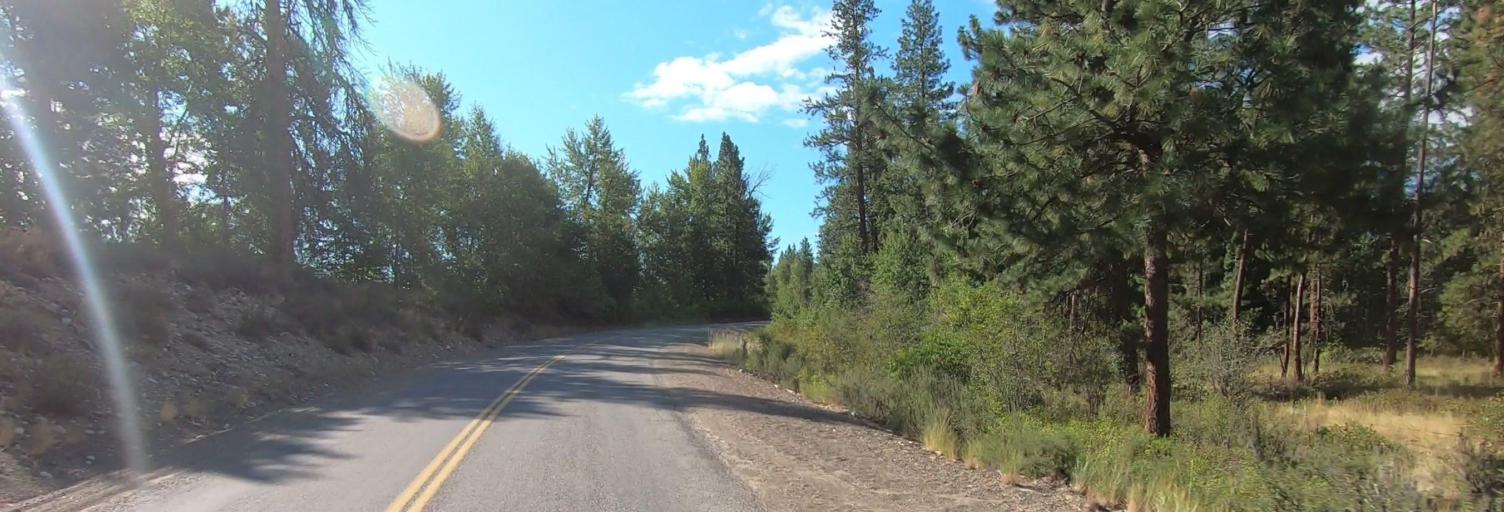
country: US
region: Washington
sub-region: Okanogan County
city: Brewster
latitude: 48.5302
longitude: -120.1781
